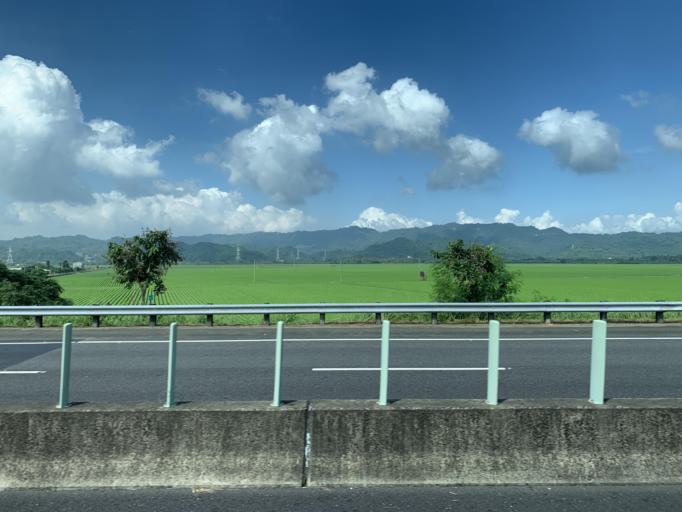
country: TW
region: Taiwan
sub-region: Pingtung
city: Pingtung
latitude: 22.8215
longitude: 120.4873
